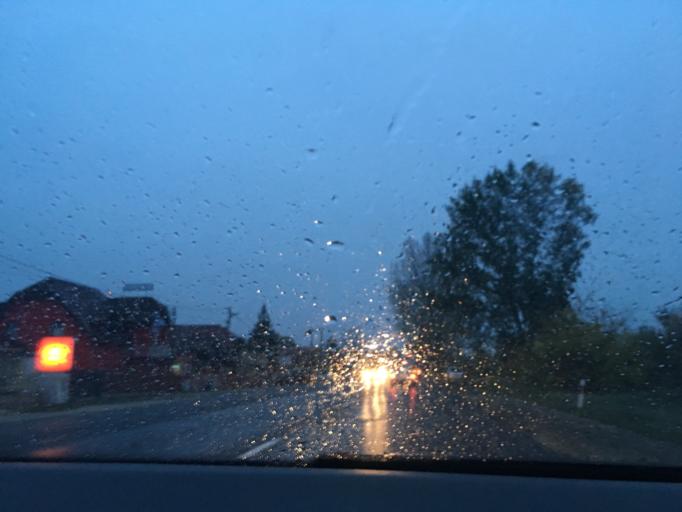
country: HU
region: Pest
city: Monor
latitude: 47.3316
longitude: 19.4470
